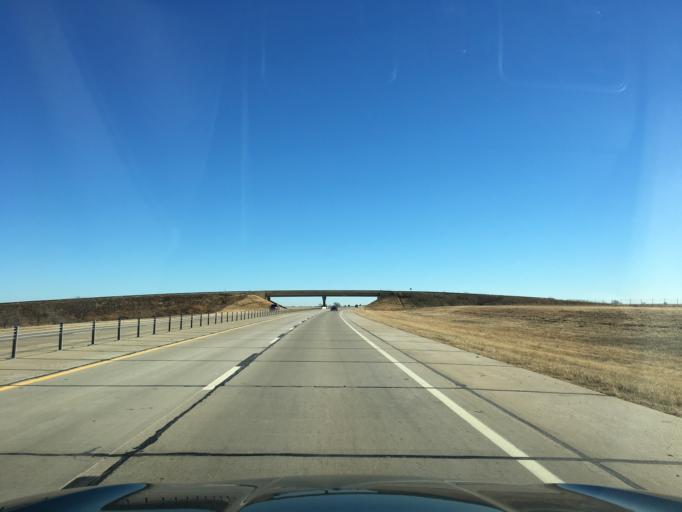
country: US
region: Oklahoma
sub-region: Noble County
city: Perry
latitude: 36.4019
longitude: -97.2499
